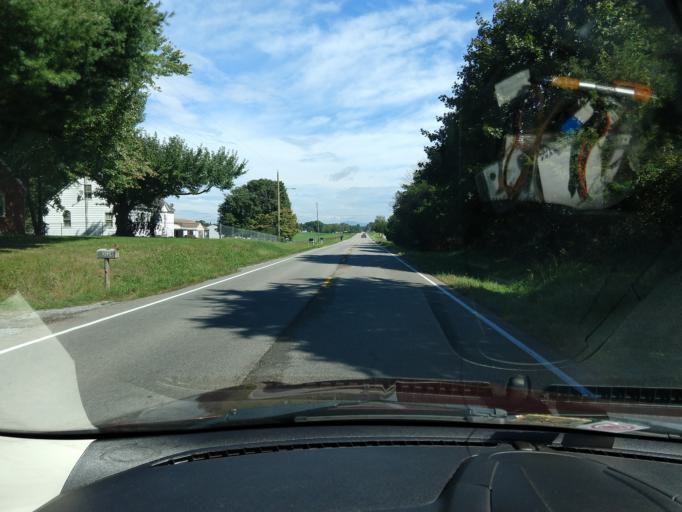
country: US
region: Virginia
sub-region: Augusta County
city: Crimora
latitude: 38.1925
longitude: -78.8389
